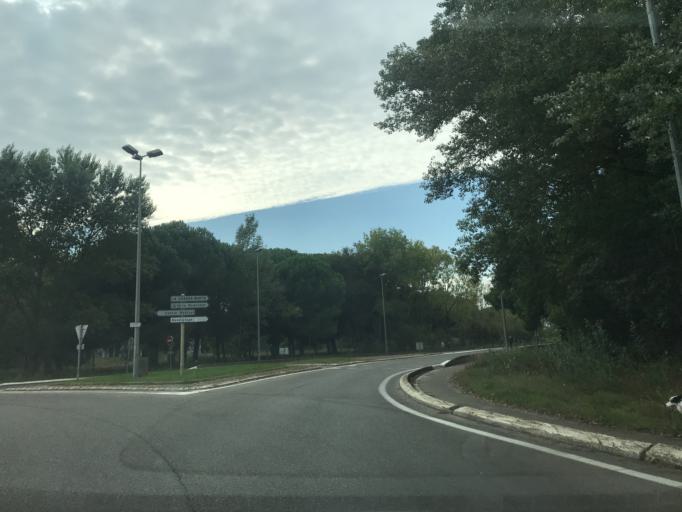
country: FR
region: Languedoc-Roussillon
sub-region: Departement du Gard
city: Le Grau-du-Roi
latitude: 43.5513
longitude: 4.1180
